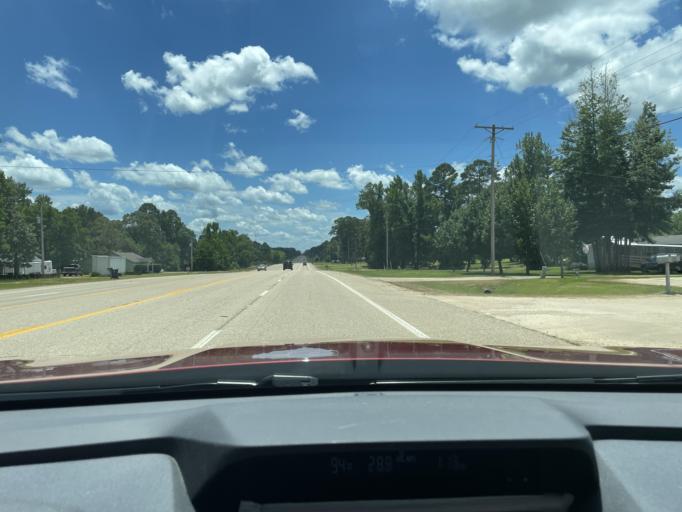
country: US
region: Arkansas
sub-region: Drew County
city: Monticello
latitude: 33.6763
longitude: -91.8048
